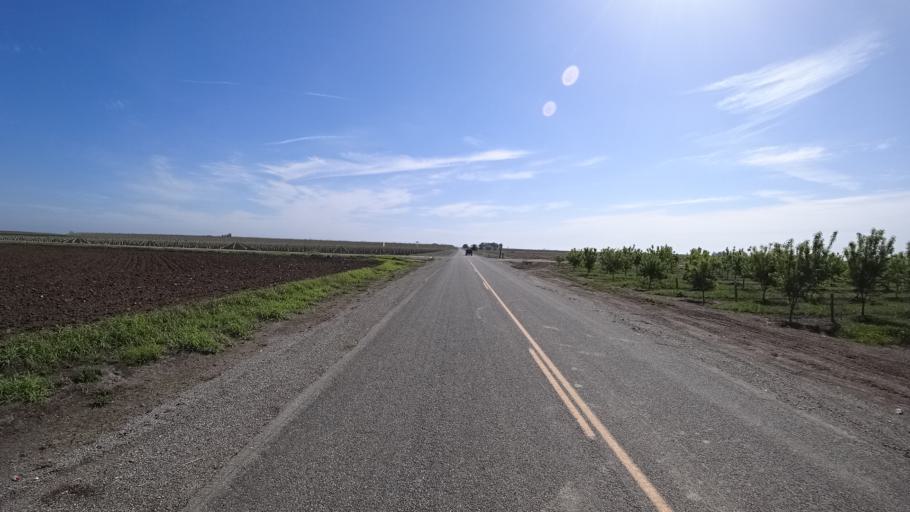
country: US
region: California
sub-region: Glenn County
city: Hamilton City
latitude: 39.6162
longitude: -122.0565
